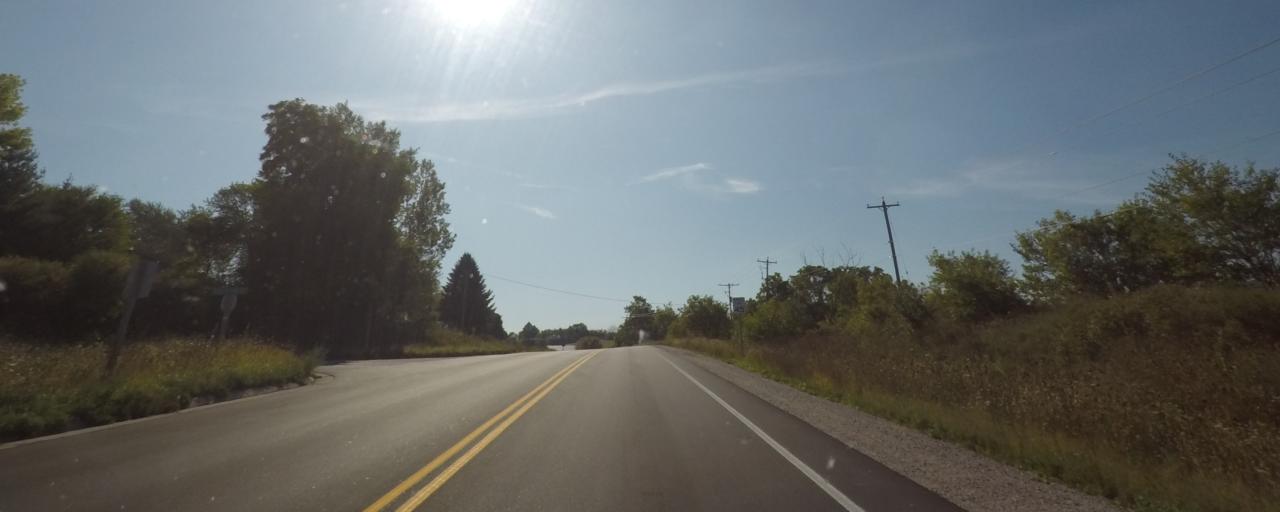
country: US
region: Wisconsin
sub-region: Jefferson County
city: Johnson Creek
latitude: 43.0178
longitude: -88.7102
